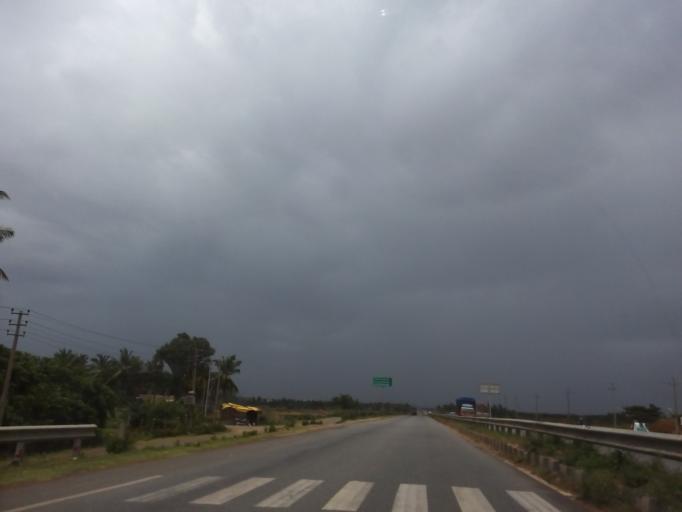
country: IN
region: Karnataka
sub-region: Davanagere
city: Harihar
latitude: 14.4511
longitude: 75.8767
